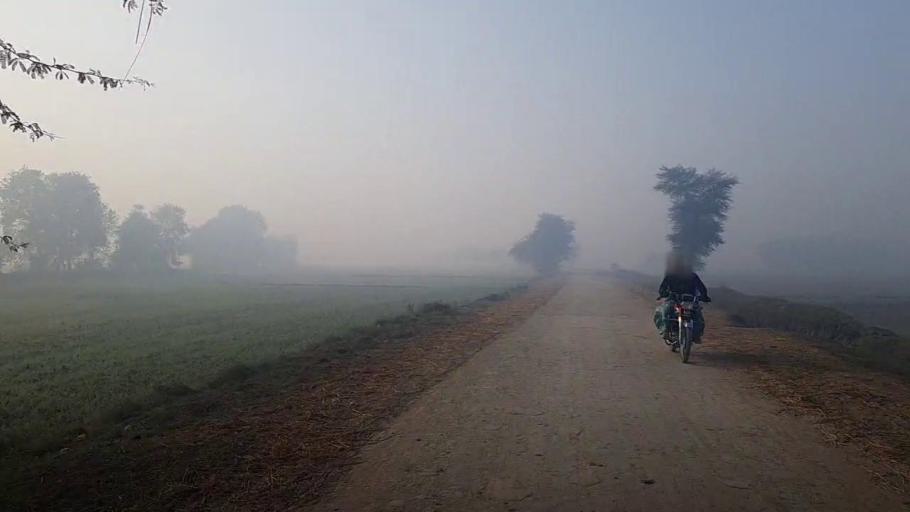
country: PK
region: Sindh
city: Mehar
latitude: 27.1630
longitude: 67.8250
